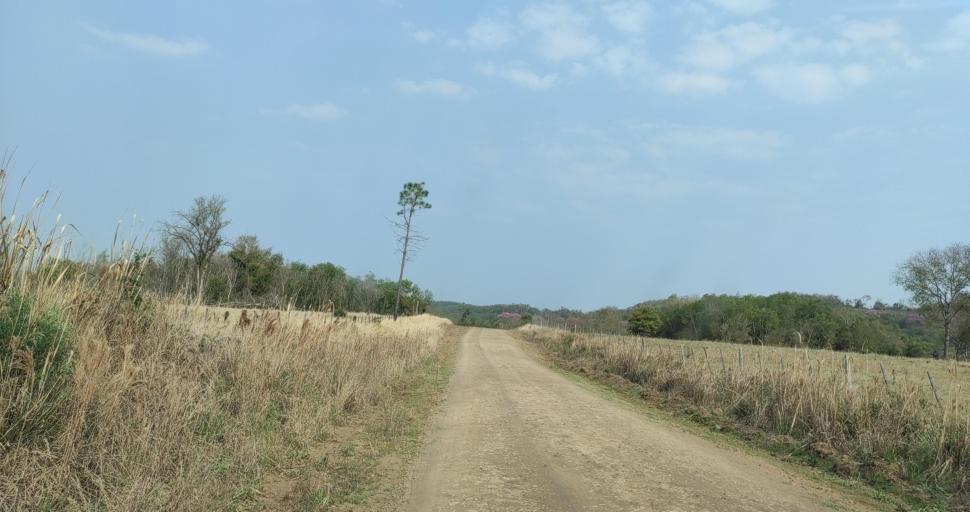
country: AR
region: Misiones
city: Cerro Azul
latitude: -27.6074
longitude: -55.5700
